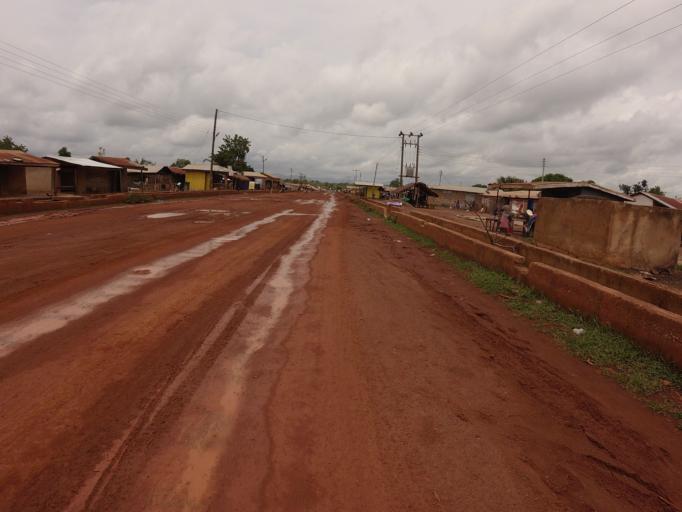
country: GH
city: Kpandae
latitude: 8.4009
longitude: 0.4048
